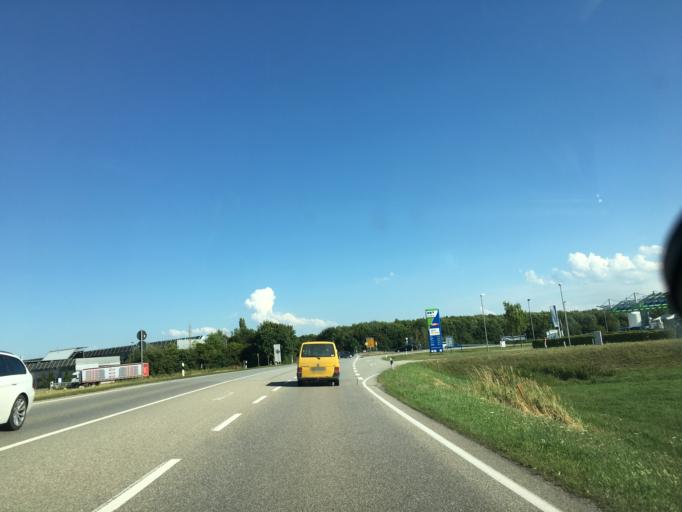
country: DE
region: Bavaria
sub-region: Upper Bavaria
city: Oberding
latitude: 48.3606
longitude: 11.8239
